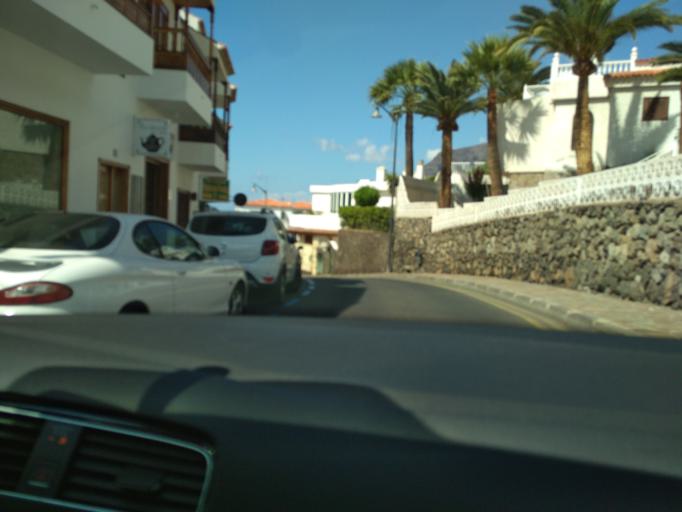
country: ES
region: Canary Islands
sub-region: Provincia de Santa Cruz de Tenerife
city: Santiago del Teide
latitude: 28.2441
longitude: -16.8398
